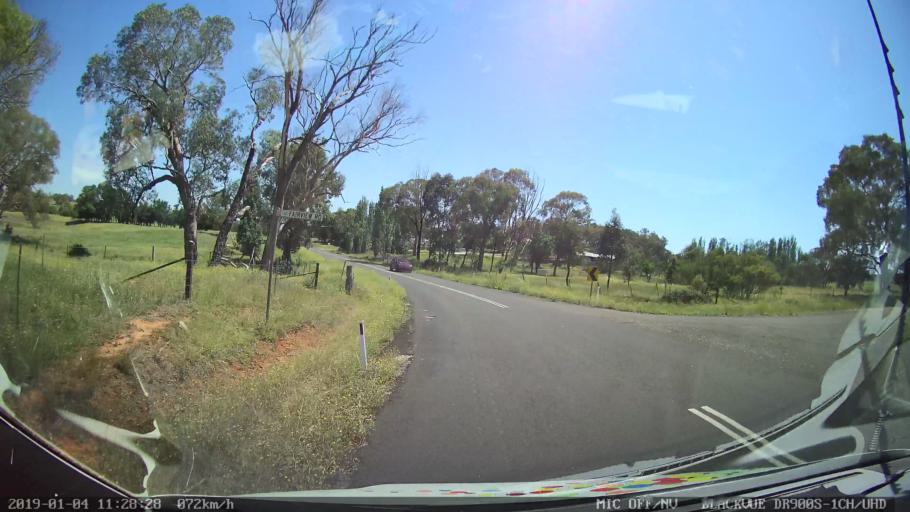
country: AU
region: New South Wales
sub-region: Cabonne
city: Molong
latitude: -33.0995
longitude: 148.7720
